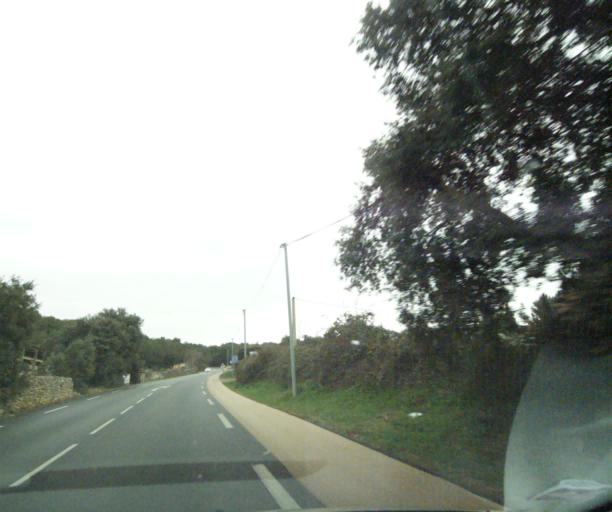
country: FR
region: Provence-Alpes-Cote d'Azur
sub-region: Departement des Bouches-du-Rhone
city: Rognes
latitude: 43.6632
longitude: 5.3350
